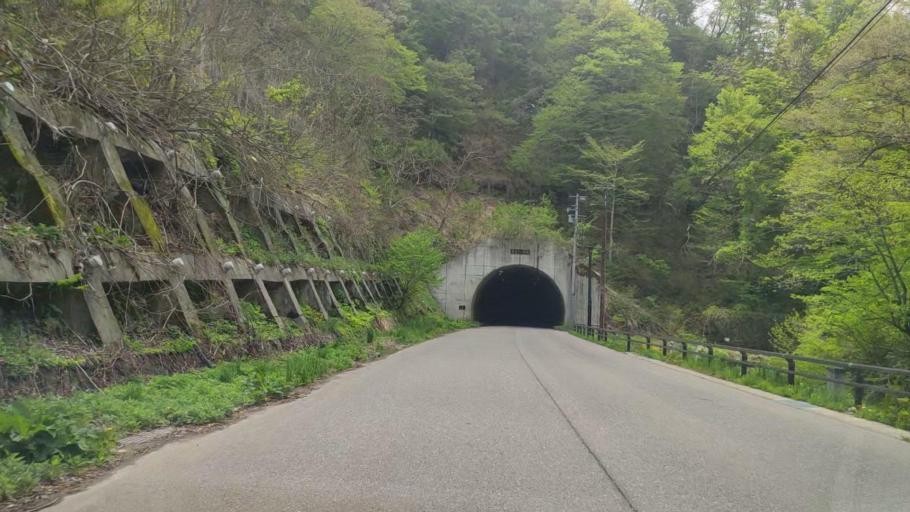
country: JP
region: Fukushima
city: Kitakata
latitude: 37.6849
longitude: 139.7203
